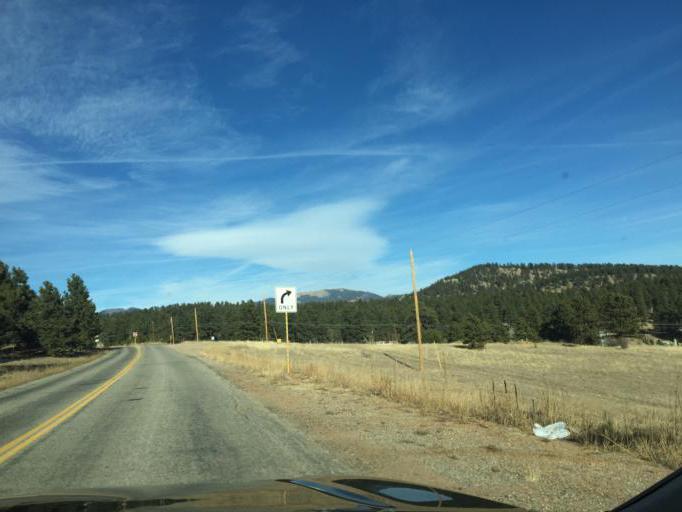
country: US
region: Colorado
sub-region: Jefferson County
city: Evergreen
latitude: 39.4396
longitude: -105.4574
